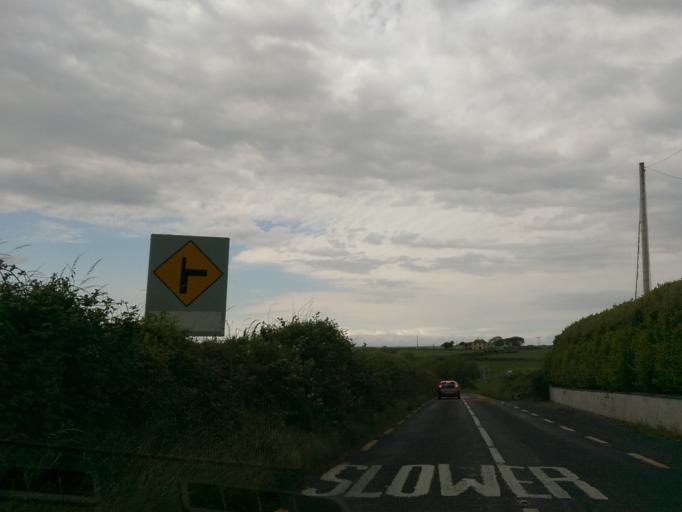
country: IE
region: Connaught
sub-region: County Galway
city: Bearna
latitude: 53.1456
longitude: -9.0793
